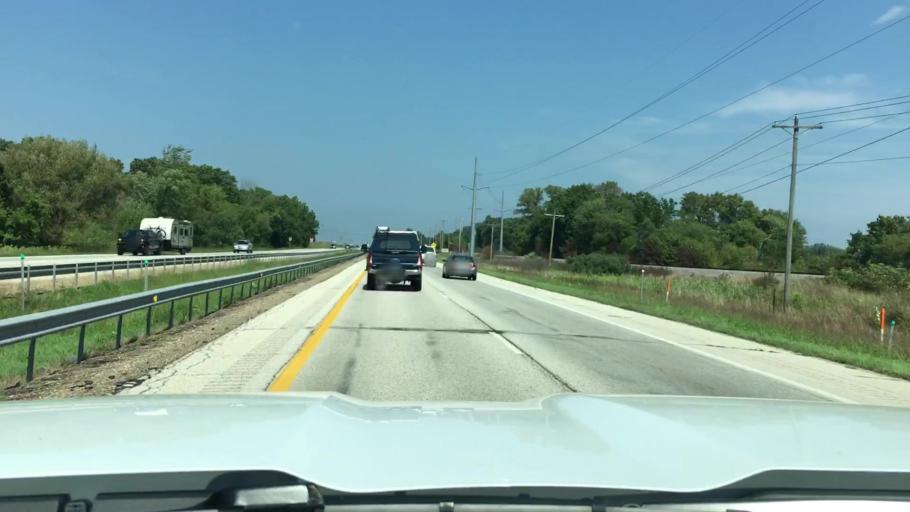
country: US
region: Michigan
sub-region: Kalamazoo County
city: Schoolcraft
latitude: 42.0599
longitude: -85.6359
